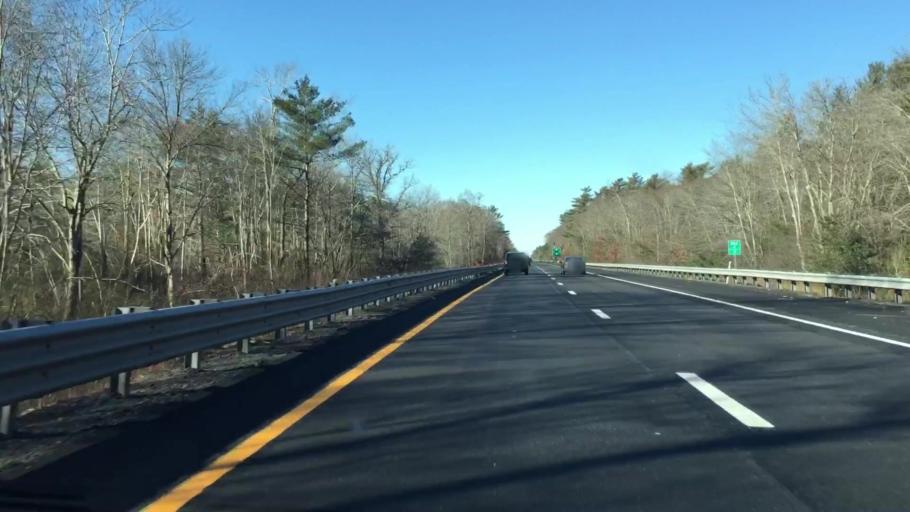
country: US
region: Massachusetts
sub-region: Plymouth County
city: West Wareham
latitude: 41.8170
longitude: -70.7988
